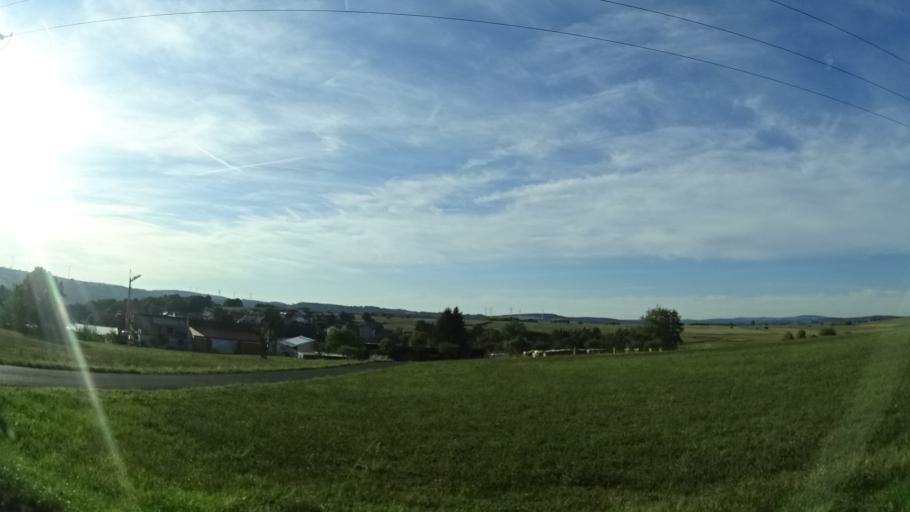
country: DE
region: Hesse
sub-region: Regierungsbezirk Darmstadt
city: Bad Soden-Salmunster
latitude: 50.3157
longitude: 9.3384
